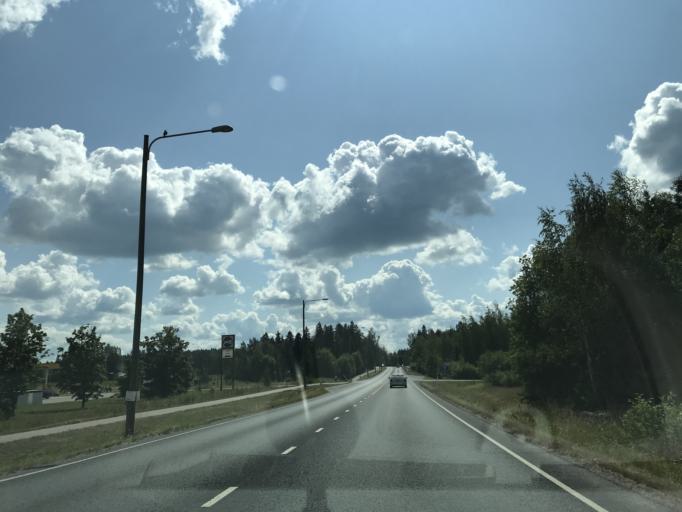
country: FI
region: Paijanne Tavastia
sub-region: Lahti
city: Orimattila
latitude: 60.8233
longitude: 25.7288
